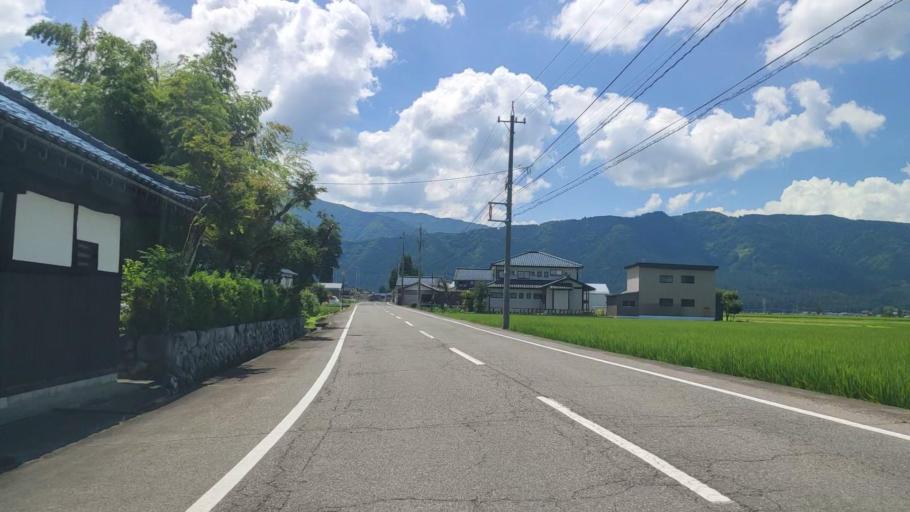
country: JP
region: Fukui
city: Ono
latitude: 35.9548
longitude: 136.5375
